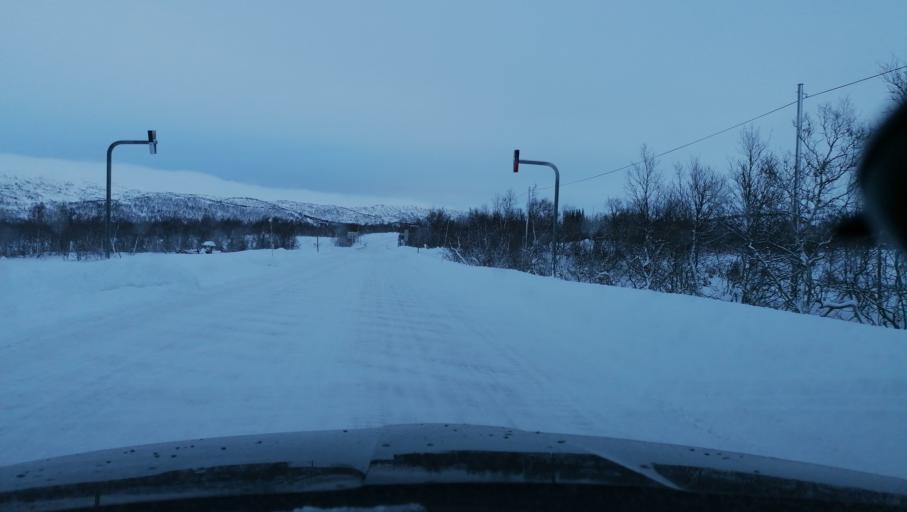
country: NO
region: Aust-Agder
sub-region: Bykle
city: Hovden
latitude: 59.6441
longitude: 7.4599
